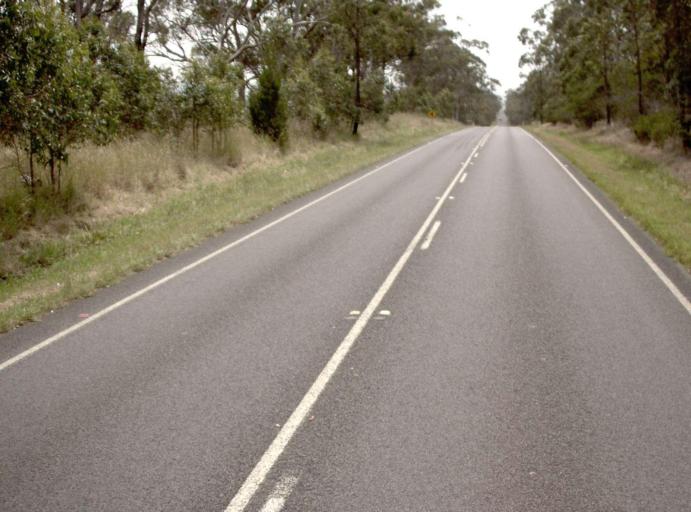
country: AU
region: Victoria
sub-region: Latrobe
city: Traralgon
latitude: -38.5172
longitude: 146.7076
